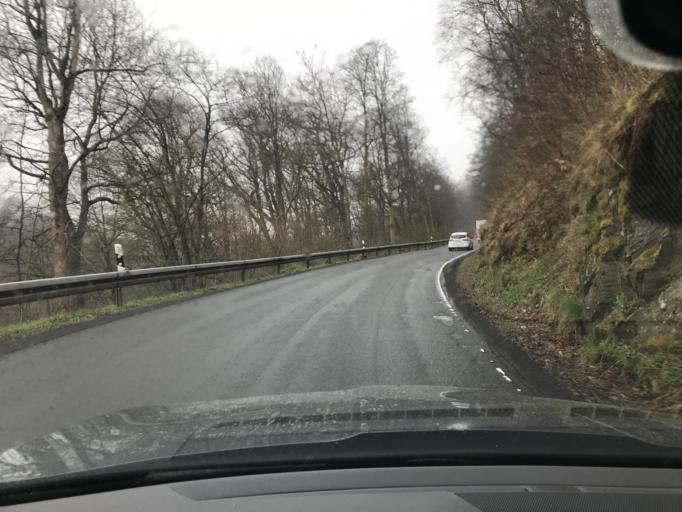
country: DE
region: Saxony-Anhalt
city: Harzgerode
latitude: 51.6667
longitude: 11.1371
